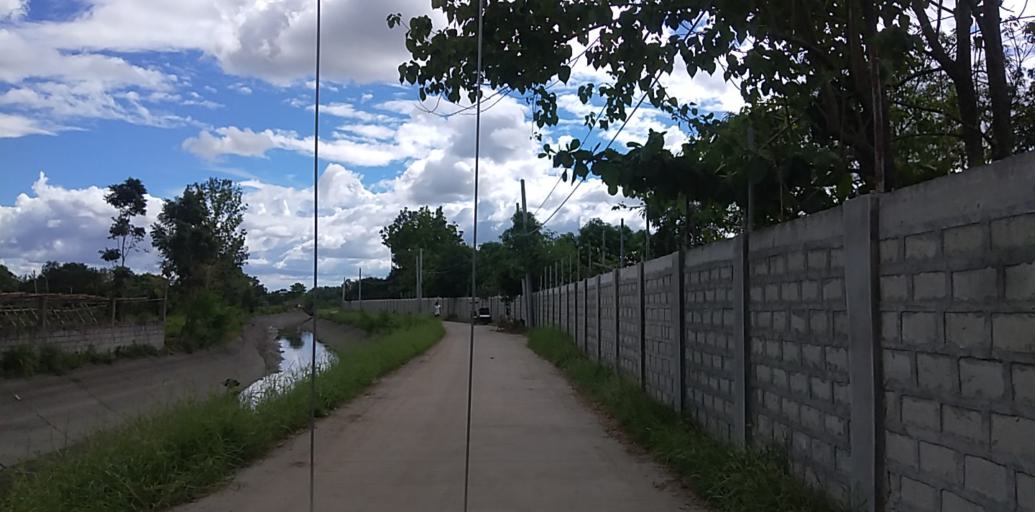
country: PH
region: Central Luzon
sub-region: Province of Pampanga
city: Arayat
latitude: 15.1377
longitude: 120.7783
